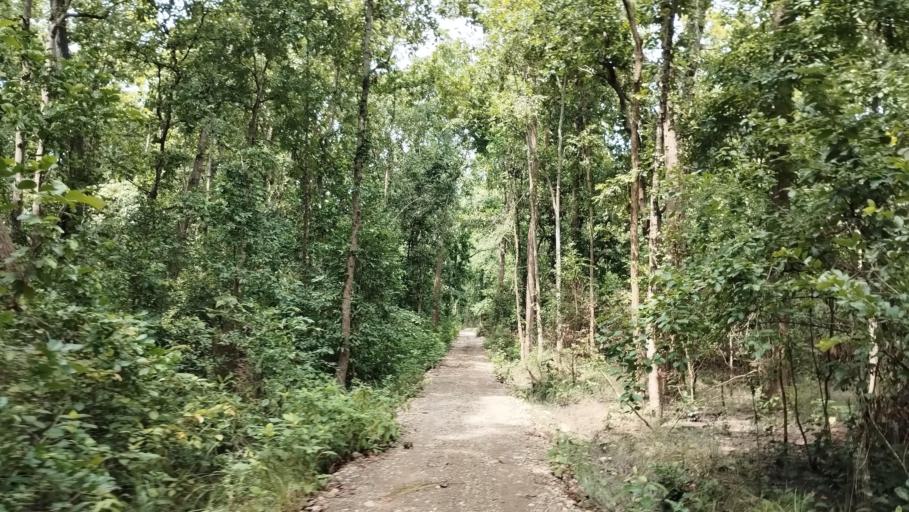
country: NP
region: Far Western
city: Tikapur
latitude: 28.4756
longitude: 81.2544
